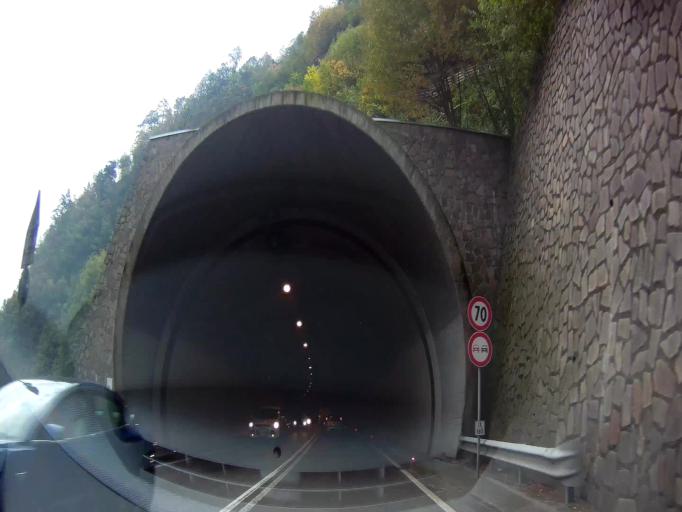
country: IT
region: Trentino-Alto Adige
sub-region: Bolzano
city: Parcines
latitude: 46.6798
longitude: 11.0963
